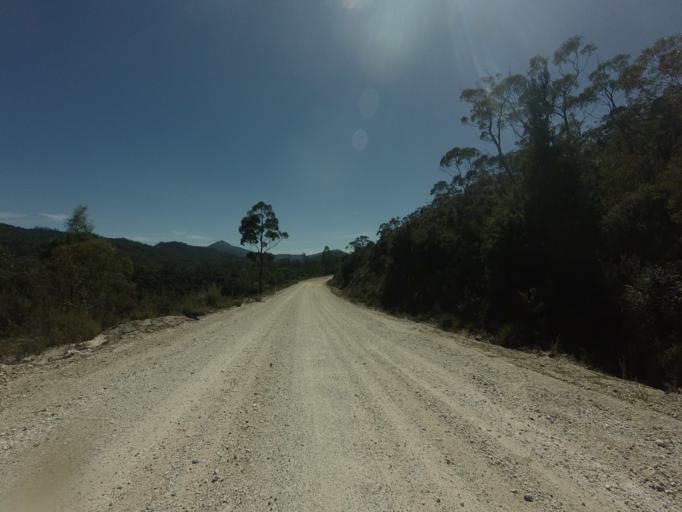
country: AU
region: Tasmania
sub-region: Huon Valley
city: Geeveston
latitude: -42.9304
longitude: 146.3414
